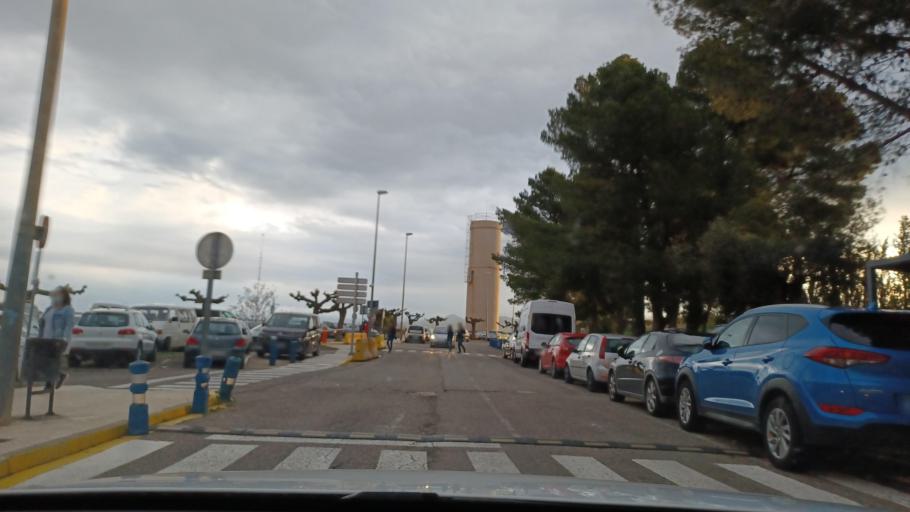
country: ES
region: Catalonia
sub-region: Provincia de Tarragona
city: Tortosa
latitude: 40.8114
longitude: 0.5251
